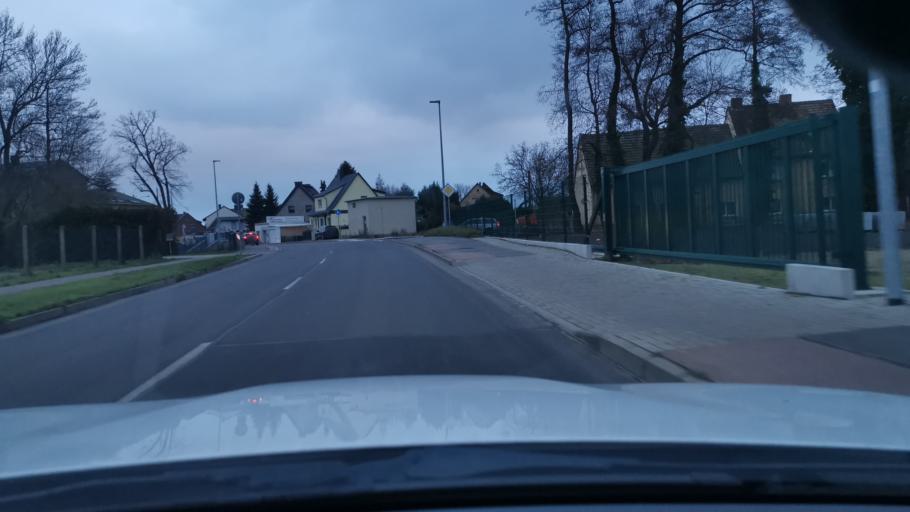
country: DE
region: Saxony-Anhalt
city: Wittenburg
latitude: 51.8768
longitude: 12.6325
